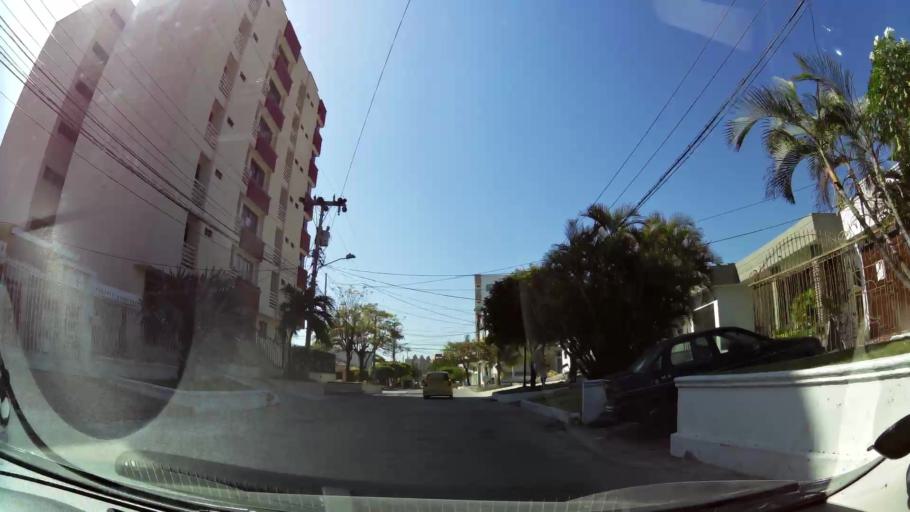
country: CO
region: Atlantico
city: Barranquilla
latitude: 10.9856
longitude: -74.8034
